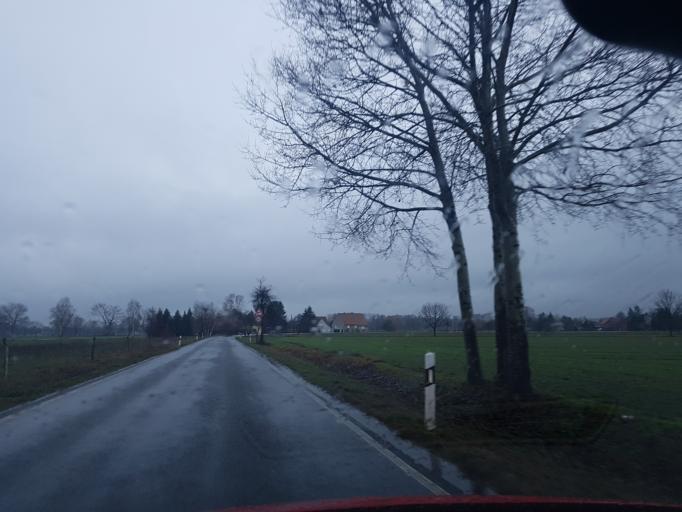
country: DE
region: Brandenburg
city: Schilda
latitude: 51.6258
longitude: 13.3164
